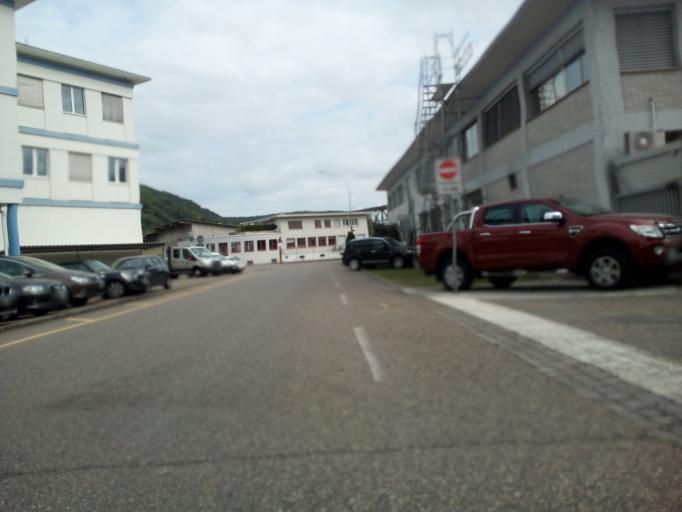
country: CH
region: Basel-Landschaft
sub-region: Bezirk Arlesheim
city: Birsfelden
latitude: 47.5553
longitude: 7.6347
